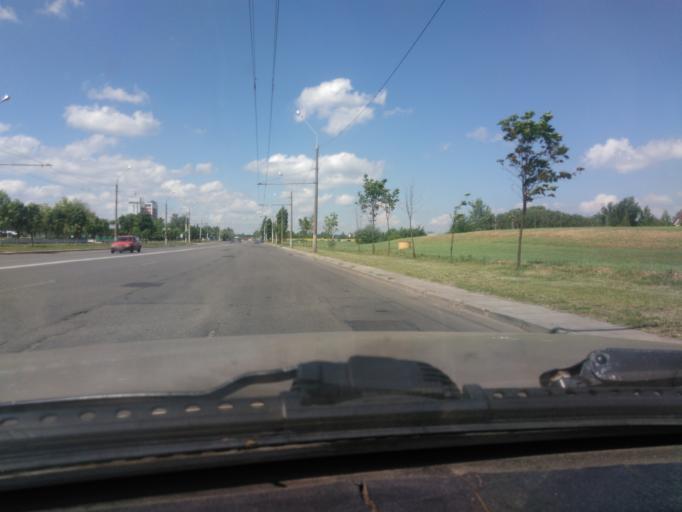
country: BY
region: Mogilev
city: Palykavichy Pyershyya
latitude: 53.9649
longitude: 30.3529
